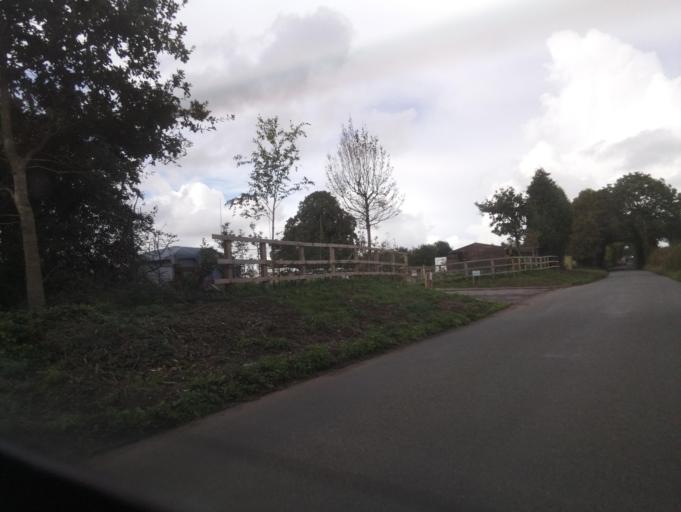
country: GB
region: England
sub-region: Worcestershire
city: Kidderminster
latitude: 52.3543
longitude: -2.1916
